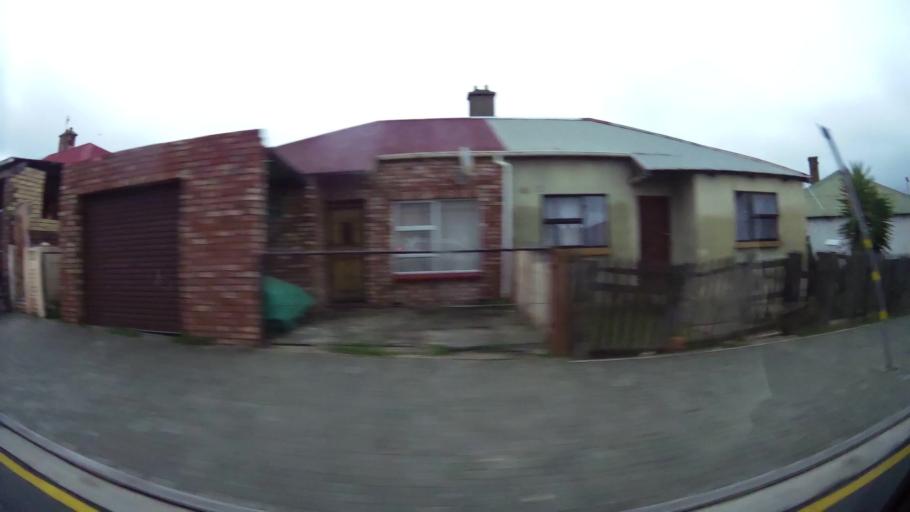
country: ZA
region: Eastern Cape
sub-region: Nelson Mandela Bay Metropolitan Municipality
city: Port Elizabeth
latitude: -33.9390
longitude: 25.5934
